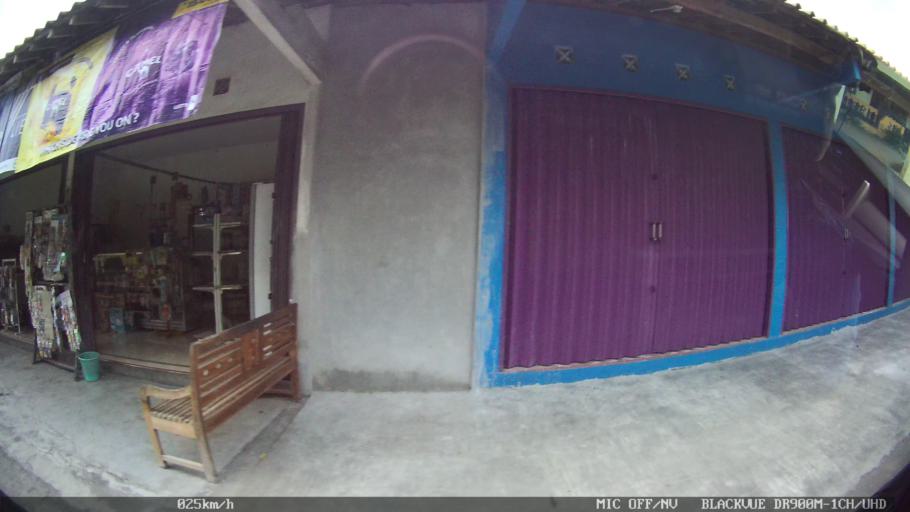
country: ID
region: Daerah Istimewa Yogyakarta
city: Gamping Lor
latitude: -7.7840
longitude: 110.3358
